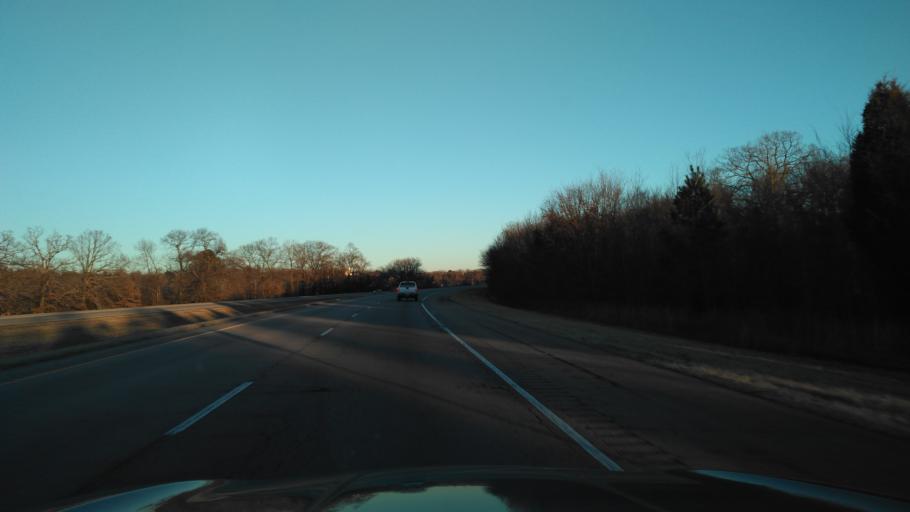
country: US
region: Arkansas
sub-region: Crawford County
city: Van Buren
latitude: 35.4629
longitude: -94.4105
